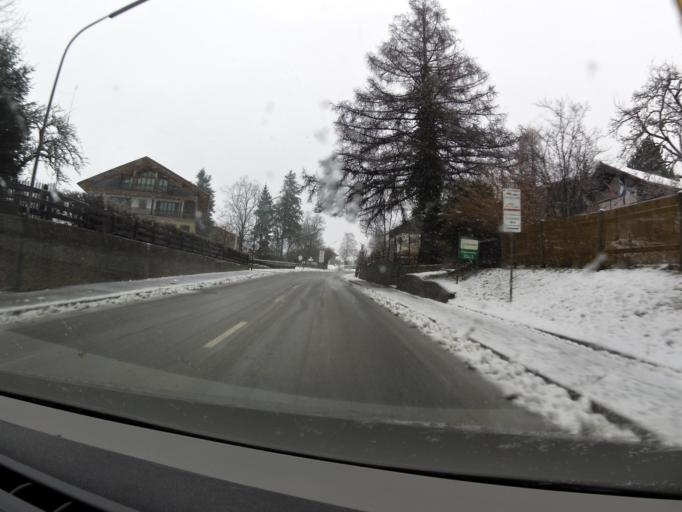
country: DE
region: Bavaria
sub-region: Upper Bavaria
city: Waakirchen
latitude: 47.7712
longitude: 11.6723
